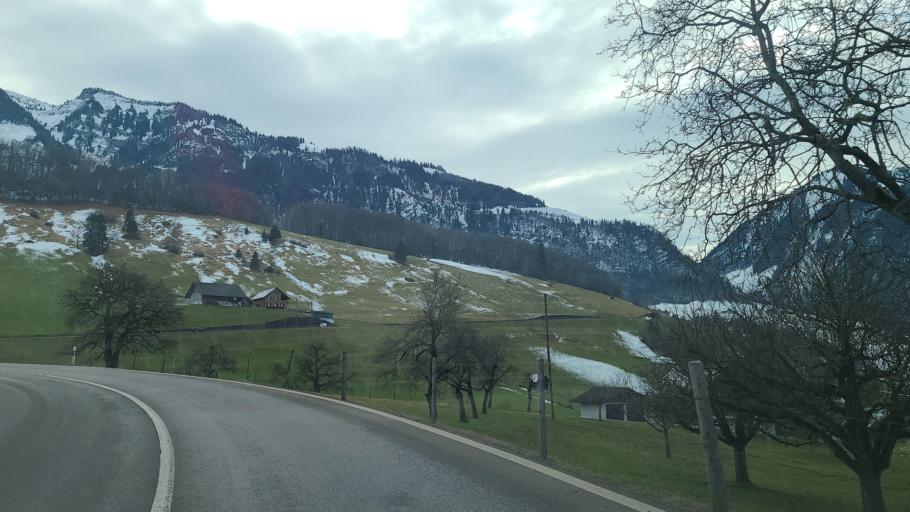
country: CH
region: Obwalden
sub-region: Obwalden
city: Kerns
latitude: 46.8892
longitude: 8.2754
